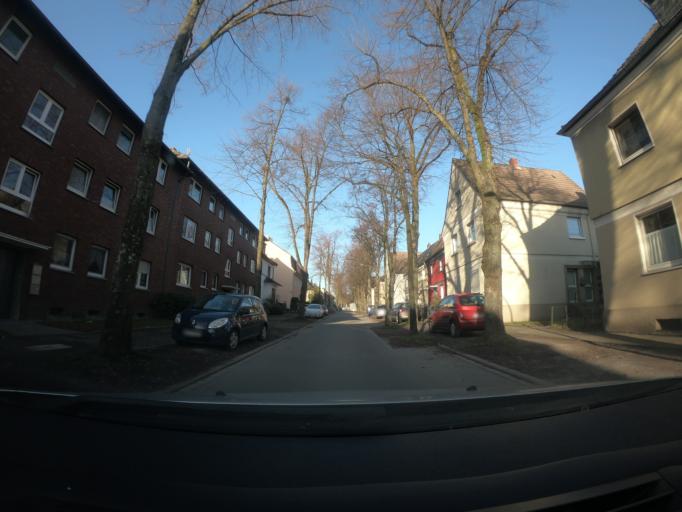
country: DE
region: North Rhine-Westphalia
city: Waltrop
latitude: 51.5981
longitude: 7.4433
